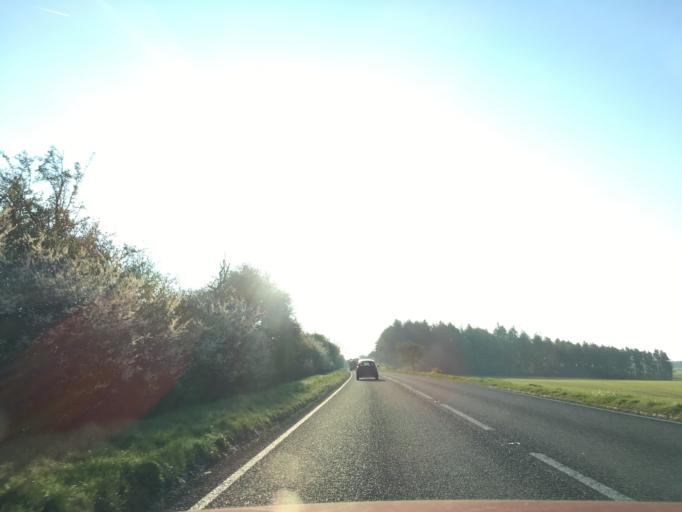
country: GB
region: England
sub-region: Gloucestershire
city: Bourton on the Water
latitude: 51.8153
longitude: -1.7467
